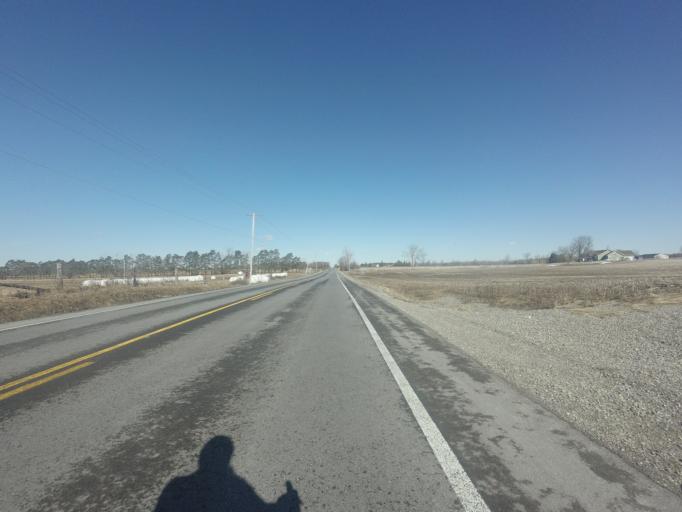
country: CA
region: Ontario
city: Carleton Place
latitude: 45.1800
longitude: -76.1079
